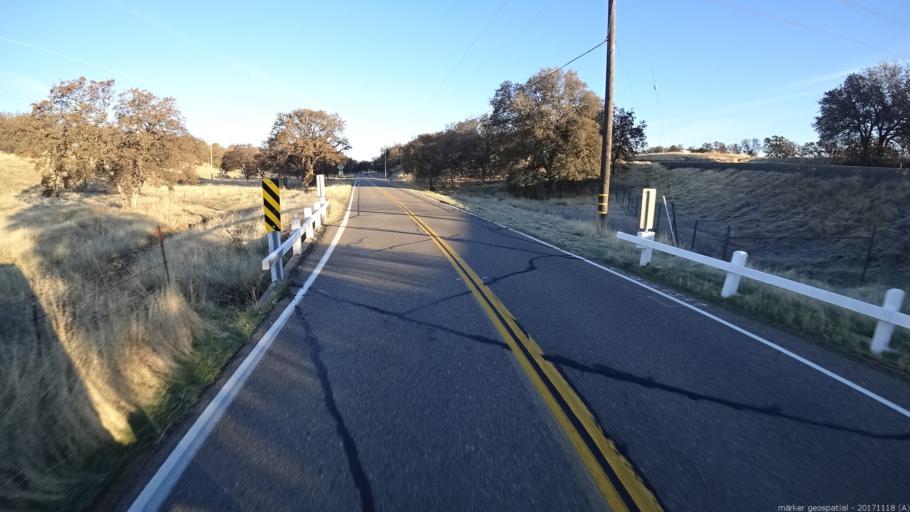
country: US
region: California
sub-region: Shasta County
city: Cottonwood
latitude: 40.4068
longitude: -122.2818
